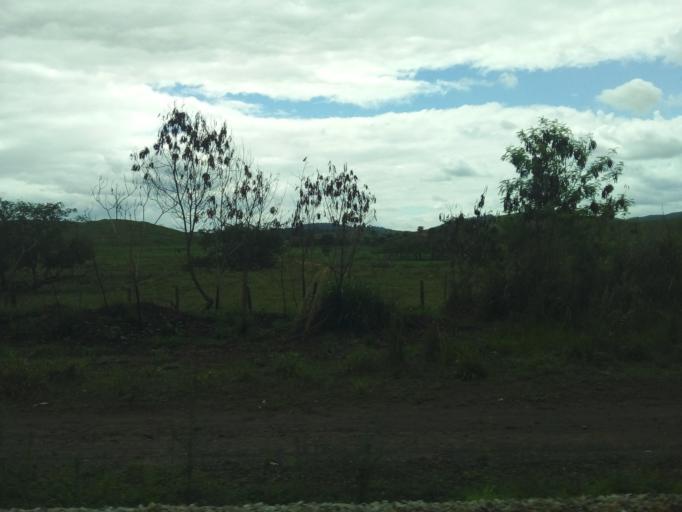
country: BR
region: Minas Gerais
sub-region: Governador Valadares
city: Governador Valadares
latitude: -19.0600
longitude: -42.1480
